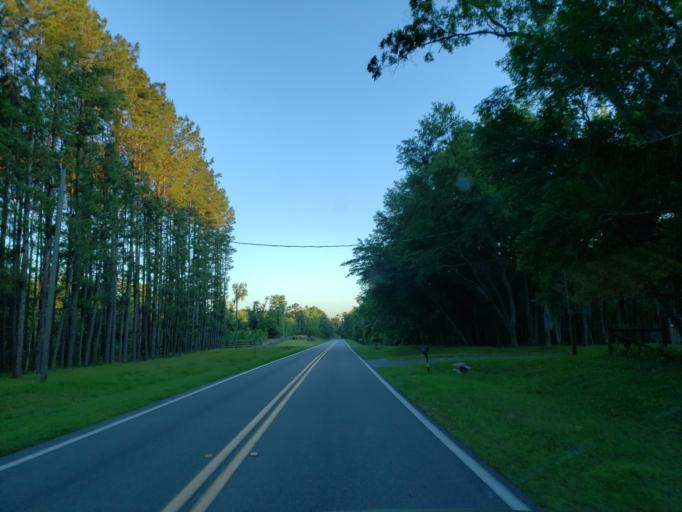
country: US
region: Florida
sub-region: Madison County
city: Madison
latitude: 30.6125
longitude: -83.2553
